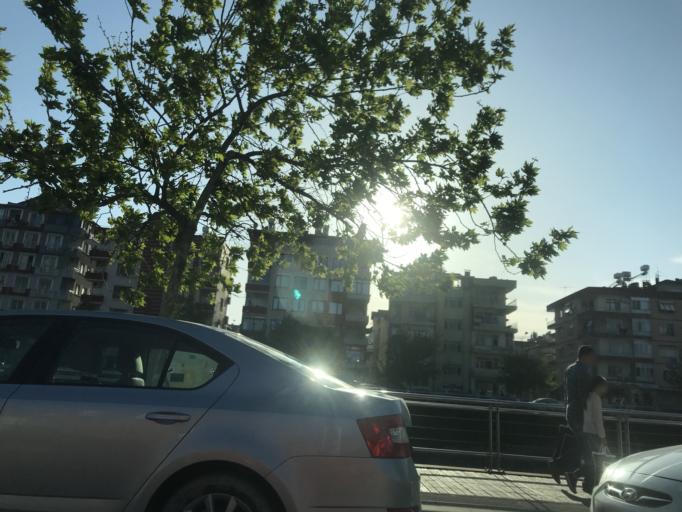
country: TR
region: Hatay
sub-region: Antakya Ilcesi
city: Antakya
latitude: 36.2083
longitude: 36.1623
